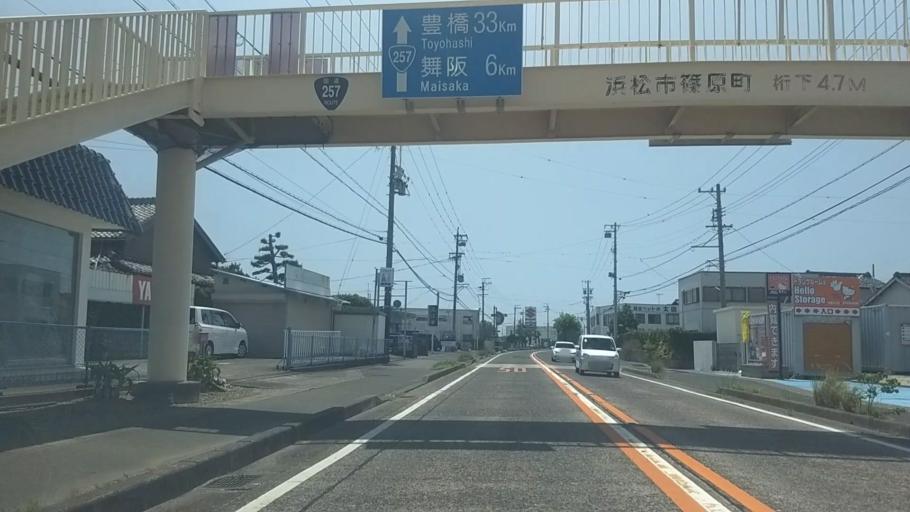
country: JP
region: Shizuoka
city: Hamamatsu
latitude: 34.6847
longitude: 137.6697
